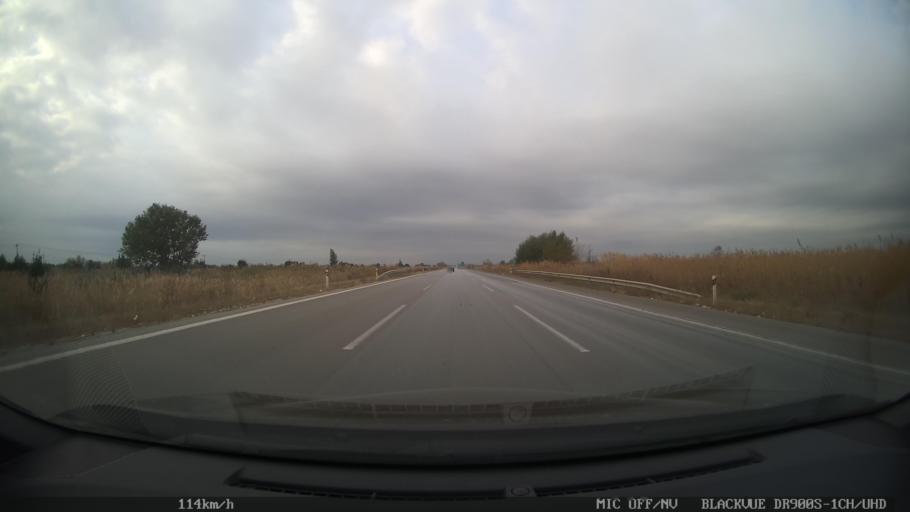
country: GR
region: Central Macedonia
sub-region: Nomos Thessalonikis
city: Chalastra
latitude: 40.6250
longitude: 22.7639
